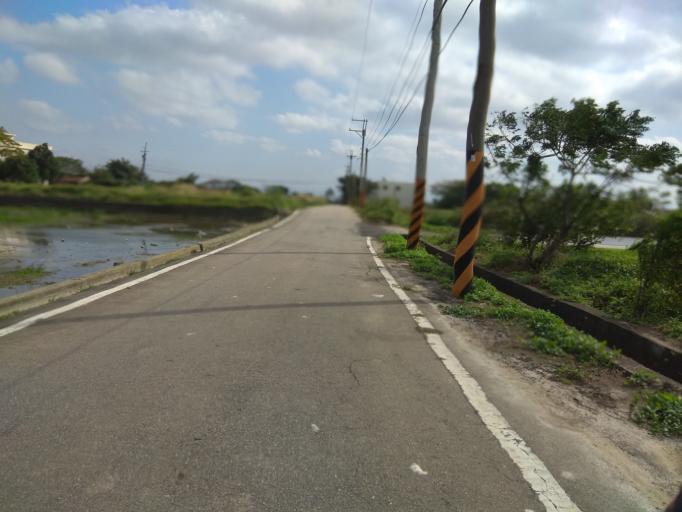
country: TW
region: Taiwan
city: Taoyuan City
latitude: 25.0620
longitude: 121.2174
